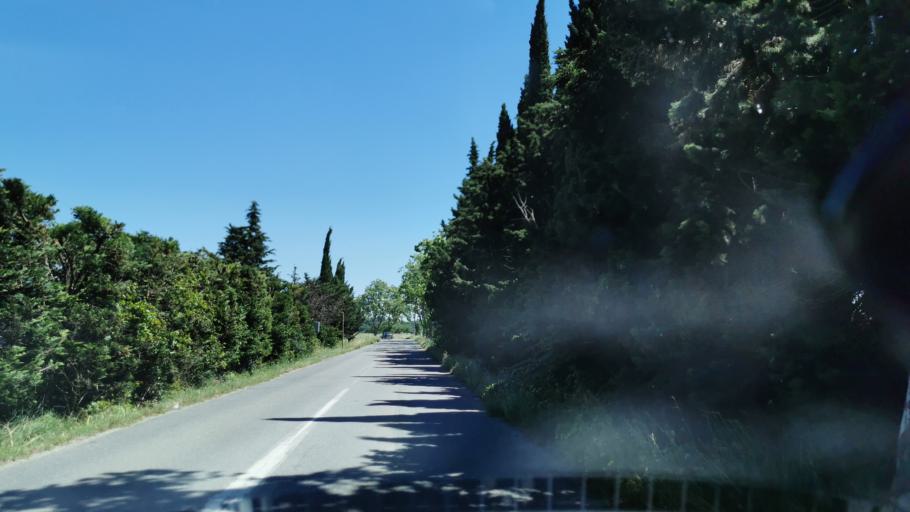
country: FR
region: Languedoc-Roussillon
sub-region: Departement de l'Aude
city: Saint-Marcel-sur-Aude
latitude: 43.2477
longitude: 2.9269
